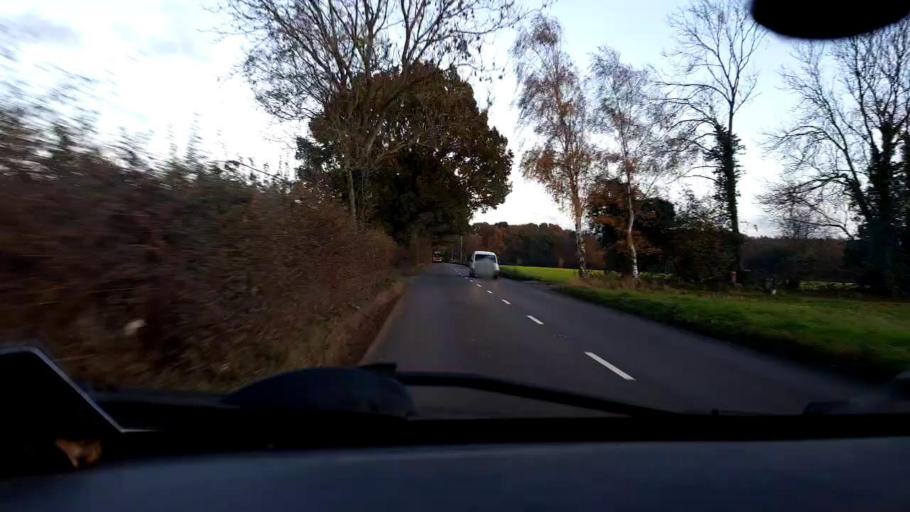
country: GB
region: England
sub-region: Norfolk
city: Mattishall
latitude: 52.6822
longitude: 1.1038
